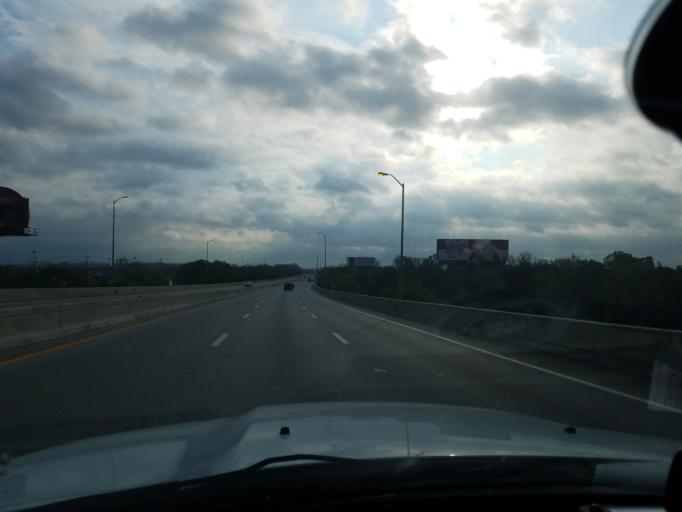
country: US
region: Indiana
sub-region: Floyd County
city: New Albany
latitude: 38.2770
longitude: -85.7978
